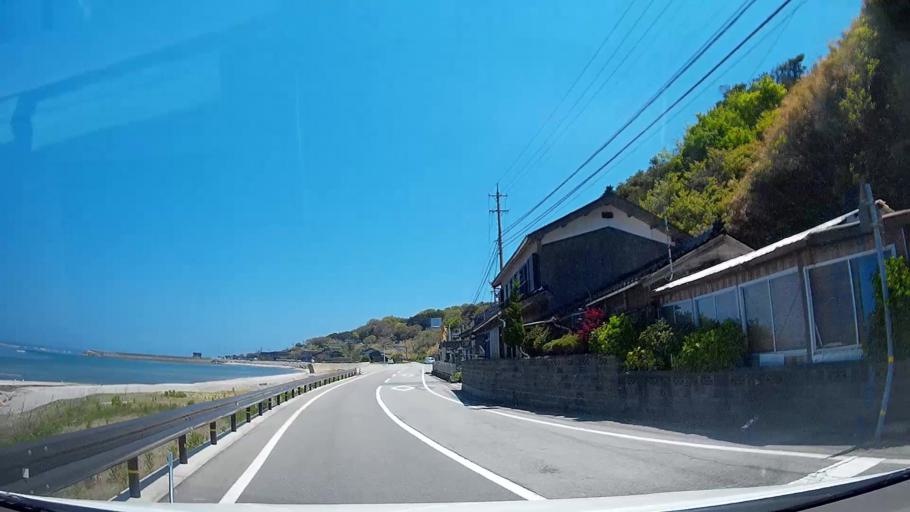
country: JP
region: Ishikawa
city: Nanao
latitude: 37.5268
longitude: 137.2827
